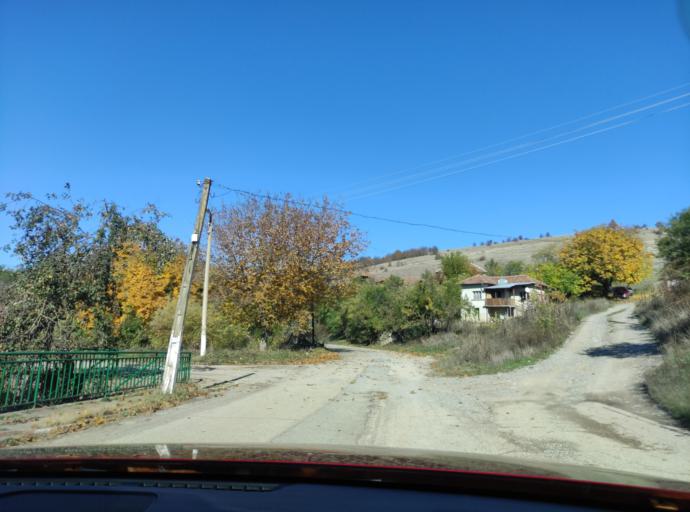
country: BG
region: Montana
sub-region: Obshtina Montana
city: Montana
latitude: 43.4355
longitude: 23.0572
